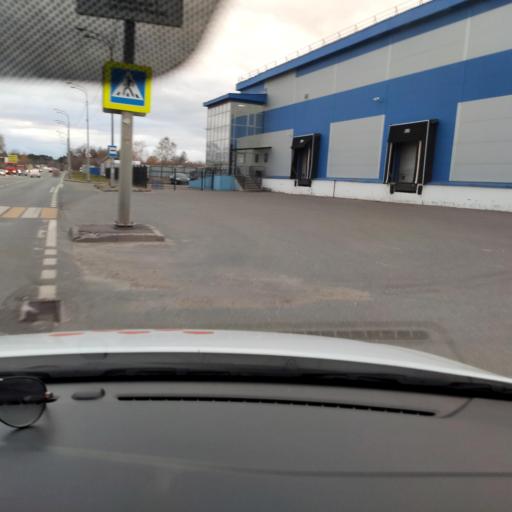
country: RU
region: Tatarstan
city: Staroye Arakchino
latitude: 55.8375
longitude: 49.0370
